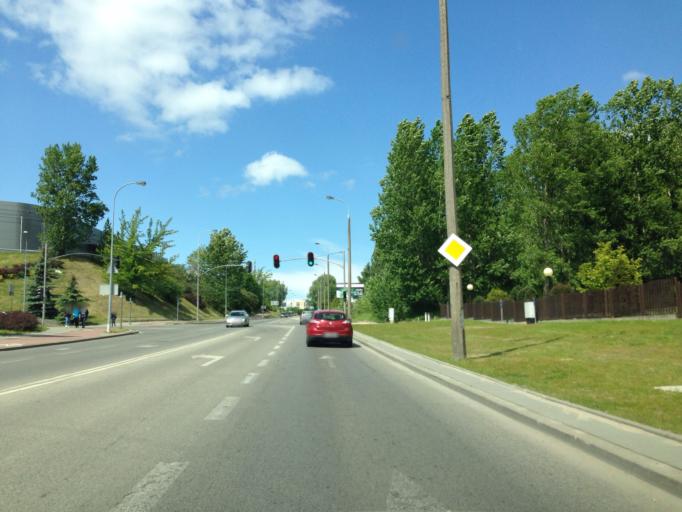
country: PL
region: Pomeranian Voivodeship
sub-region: Gdansk
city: Gdansk
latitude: 54.3507
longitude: 18.5968
